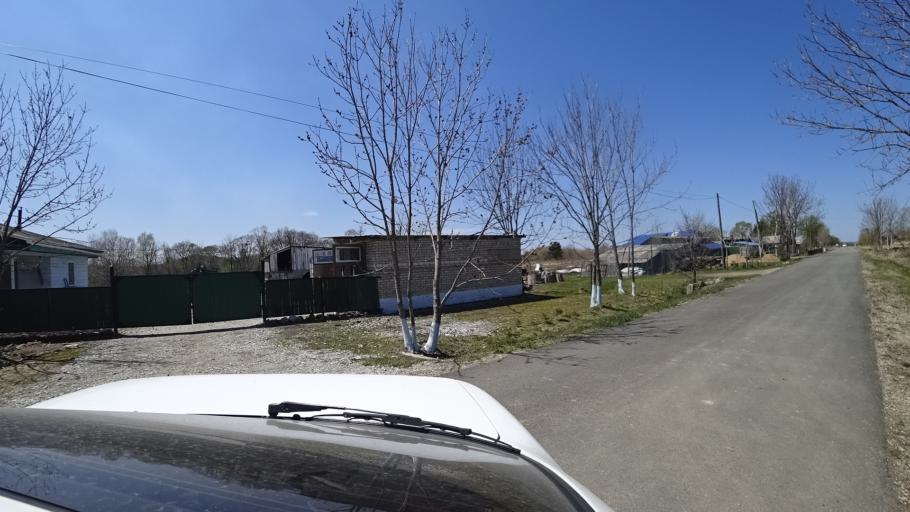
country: RU
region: Primorskiy
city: Dal'nerechensk
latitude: 45.7911
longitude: 133.7731
